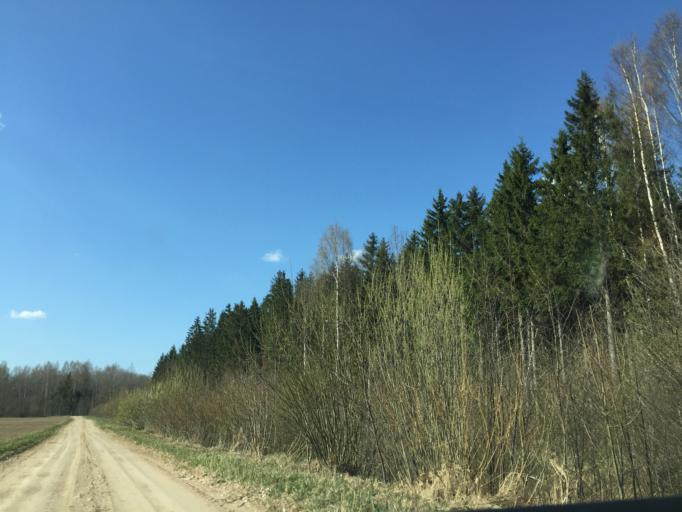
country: LV
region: Kegums
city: Kegums
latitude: 56.8396
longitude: 24.7966
